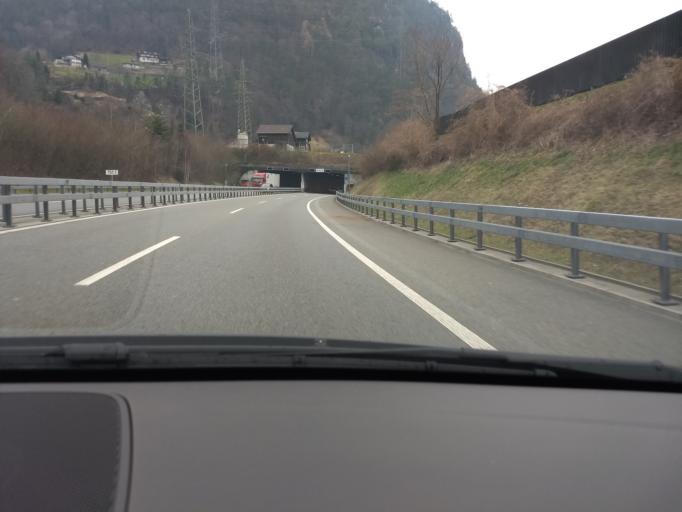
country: CH
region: Uri
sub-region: Uri
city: Erstfeld
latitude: 46.8171
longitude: 8.6441
